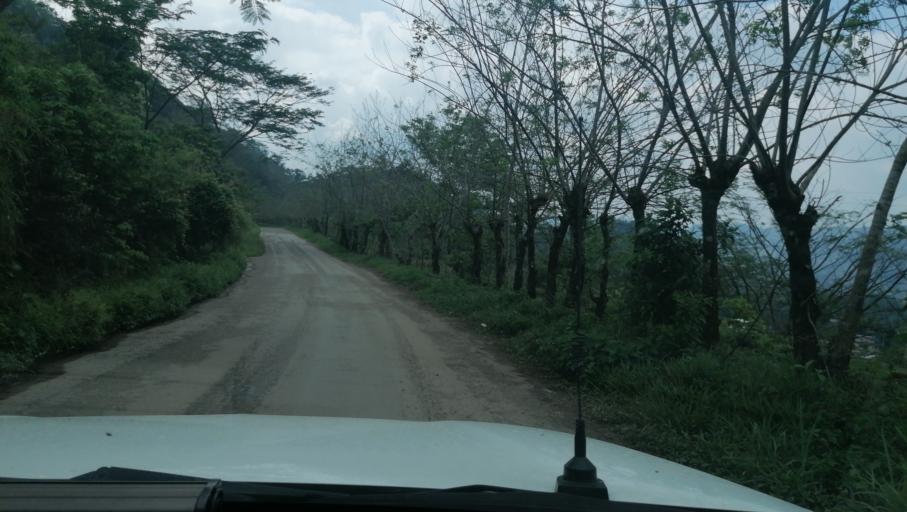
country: MX
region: Chiapas
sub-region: Francisco Leon
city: San Miguel la Sardina
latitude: 17.2371
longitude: -93.3094
